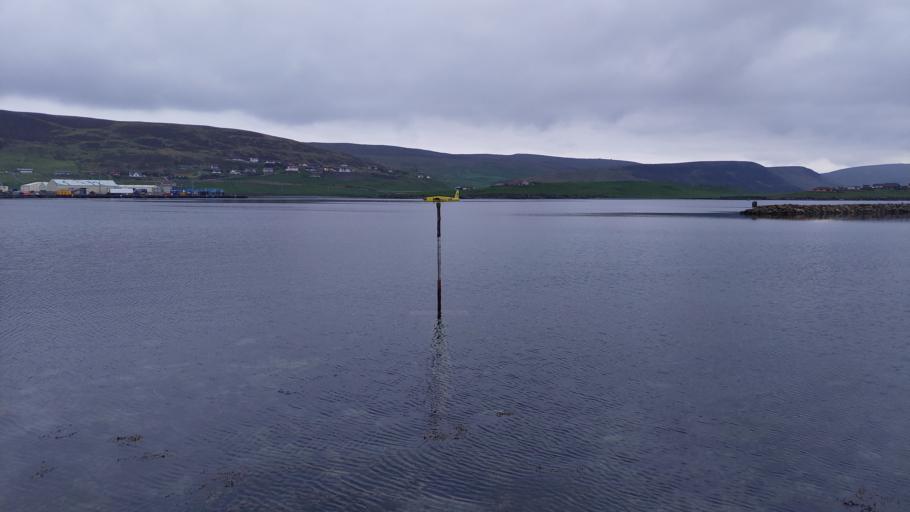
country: GB
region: Scotland
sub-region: Shetland Islands
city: Lerwick
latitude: 60.1363
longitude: -1.2842
